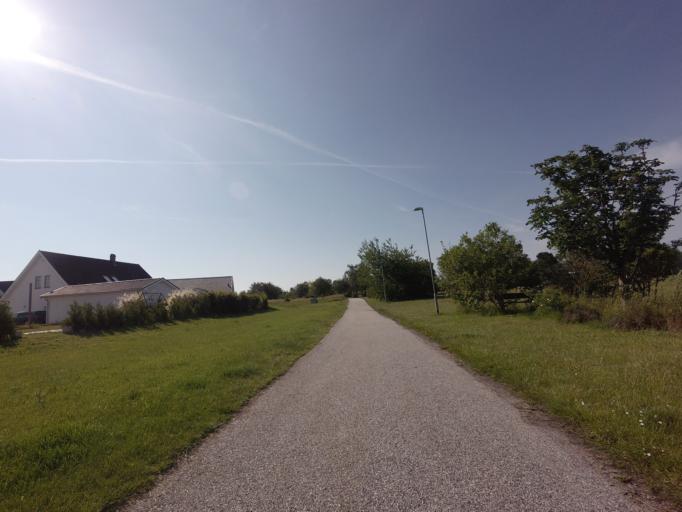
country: SE
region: Skane
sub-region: Malmo
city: Oxie
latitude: 55.4938
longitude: 13.1089
